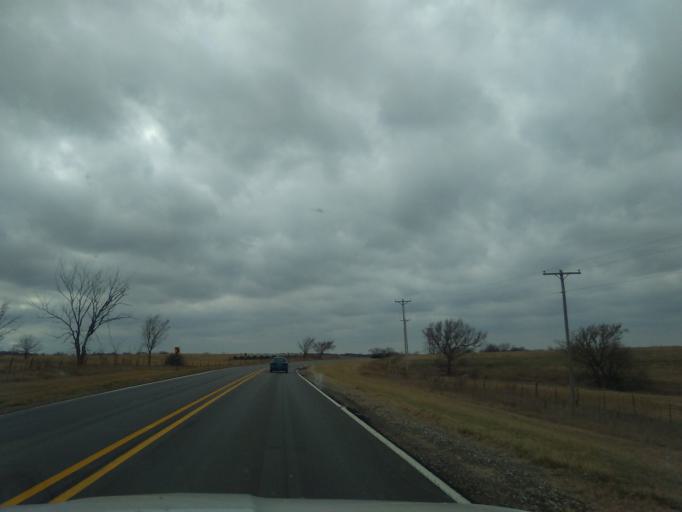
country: US
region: Nebraska
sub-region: Pawnee County
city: Pawnee City
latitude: 40.0536
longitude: -95.9773
